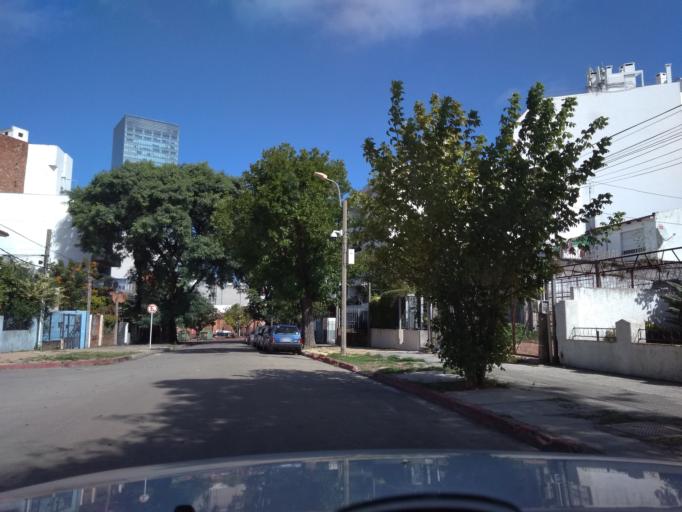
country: UY
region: Montevideo
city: Montevideo
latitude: -34.9012
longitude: -56.1367
